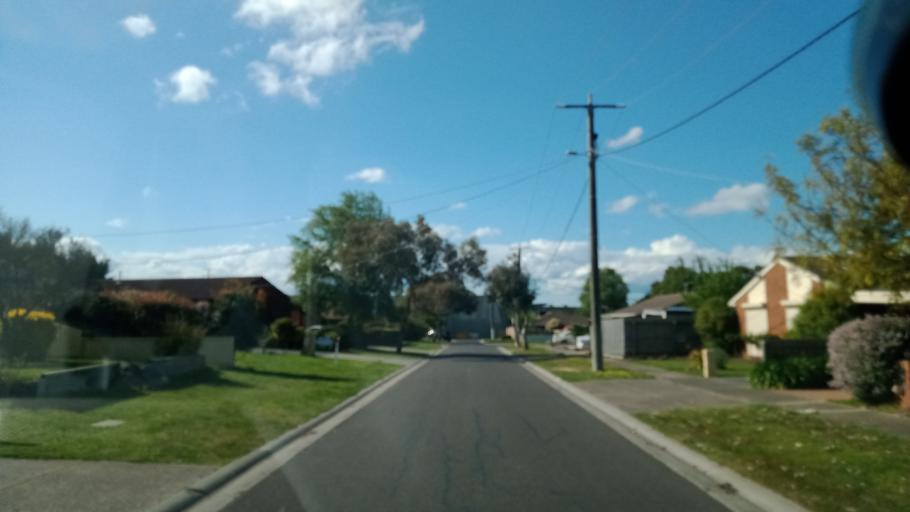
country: AU
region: Victoria
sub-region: Casey
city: Cranbourne West
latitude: -38.1044
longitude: 145.2651
